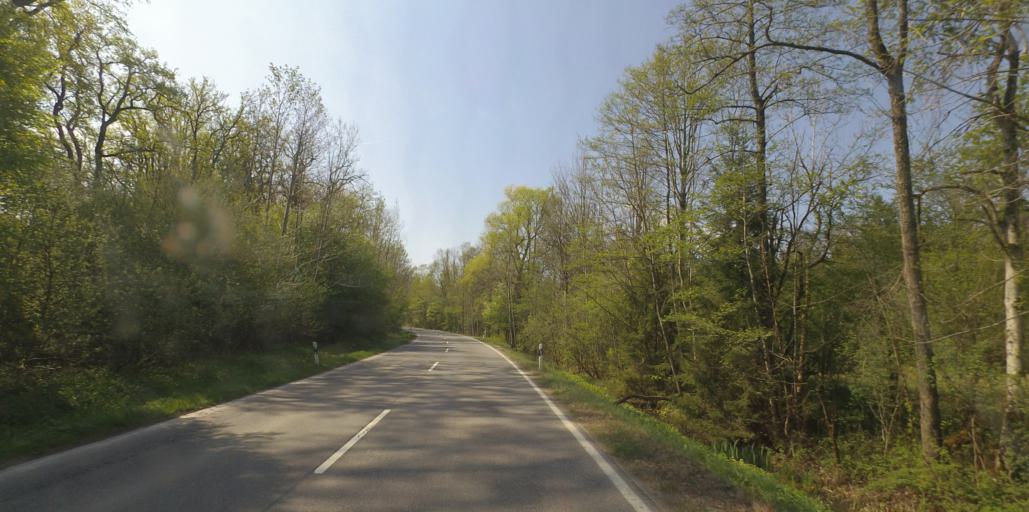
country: DE
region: Bavaria
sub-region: Upper Bavaria
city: Ubersee
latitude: 47.8260
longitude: 12.5117
